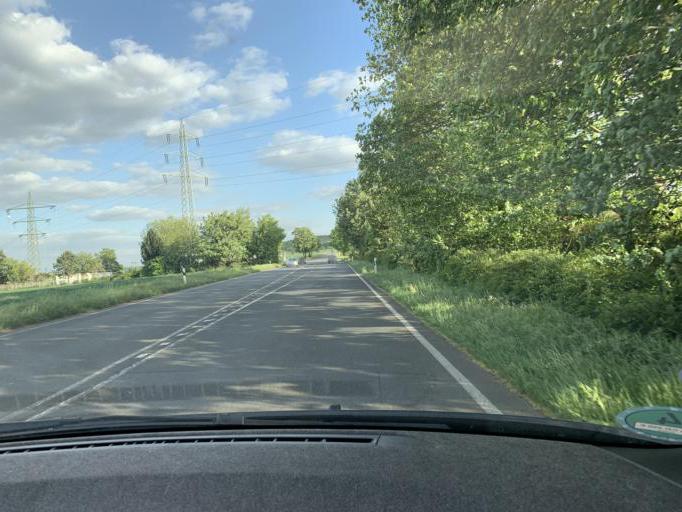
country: DE
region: North Rhine-Westphalia
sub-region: Regierungsbezirk Koln
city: Kreuzau
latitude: 50.7629
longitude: 6.4670
